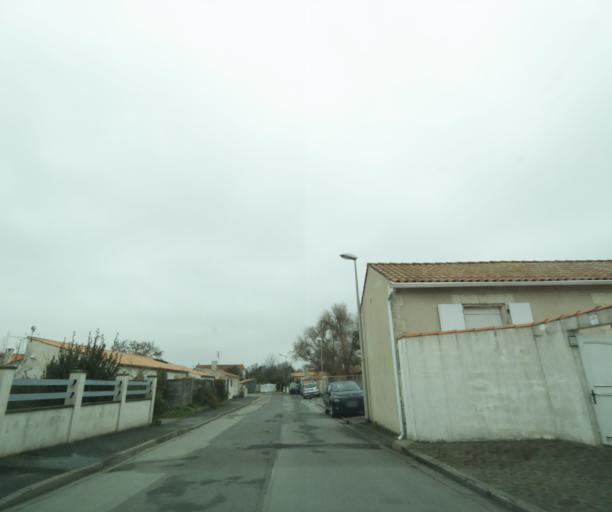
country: FR
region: Poitou-Charentes
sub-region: Departement de la Charente-Maritime
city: Lagord
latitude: 46.1833
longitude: -1.1402
